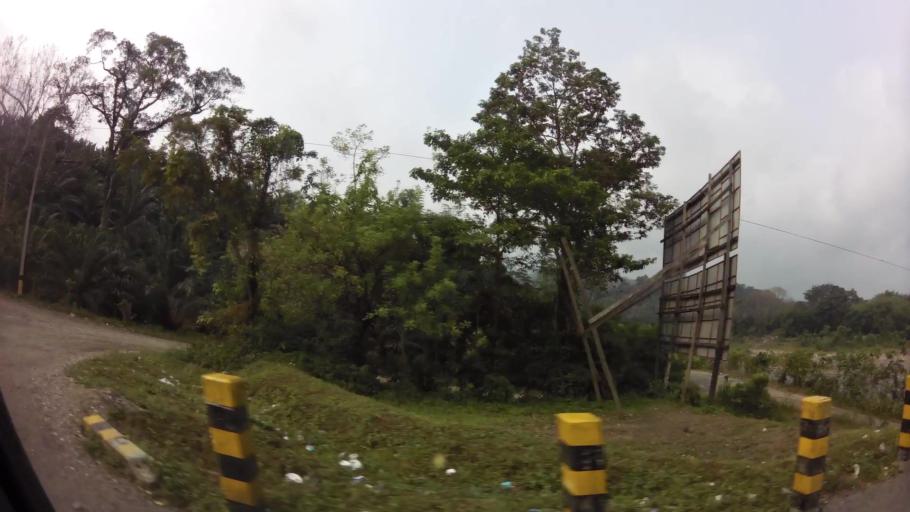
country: HN
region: Yoro
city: Toyos
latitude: 15.5135
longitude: -87.6671
